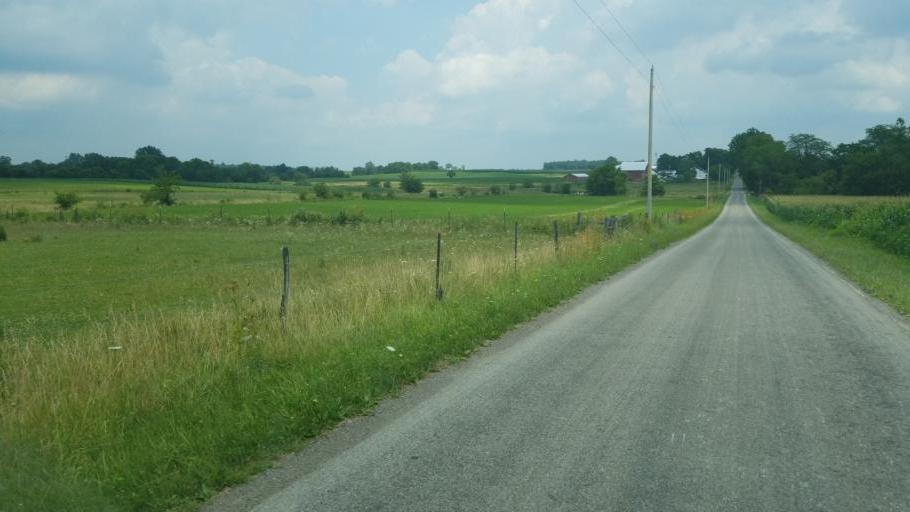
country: US
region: Ohio
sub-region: Hardin County
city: Kenton
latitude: 40.5933
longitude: -83.6243
